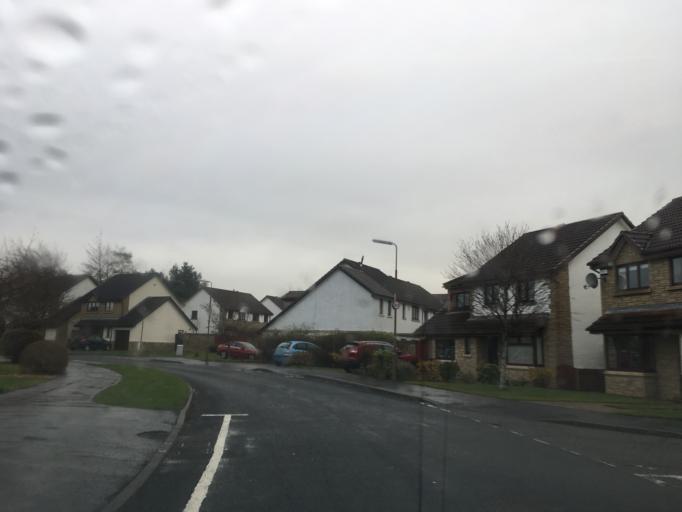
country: GB
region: Scotland
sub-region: Edinburgh
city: Currie
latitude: 55.9367
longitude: -3.3076
